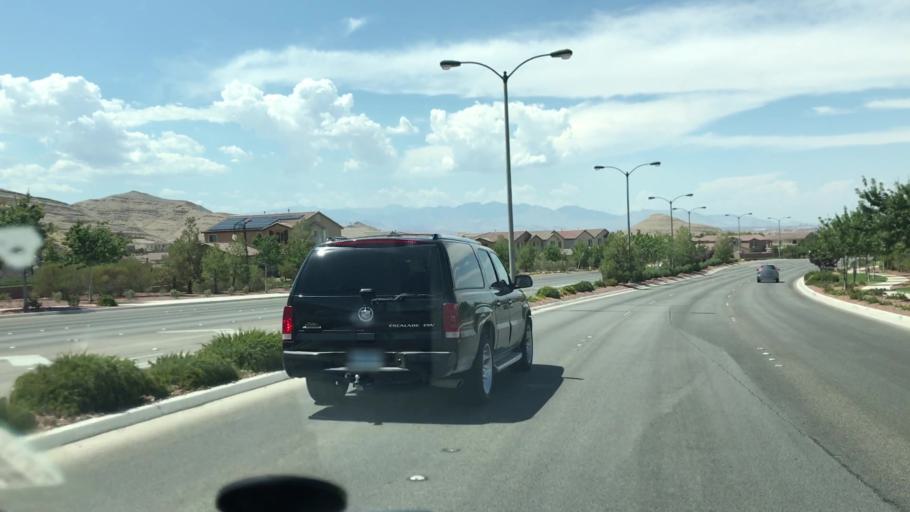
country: US
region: Nevada
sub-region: Clark County
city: Enterprise
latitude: 35.9634
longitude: -115.1860
